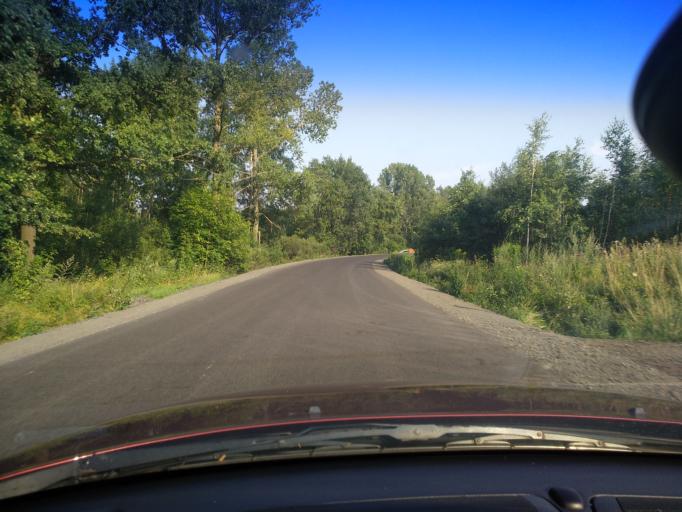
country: PL
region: Lower Silesian Voivodeship
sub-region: Powiat lubanski
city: Siekierczyn
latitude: 51.0534
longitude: 15.1914
